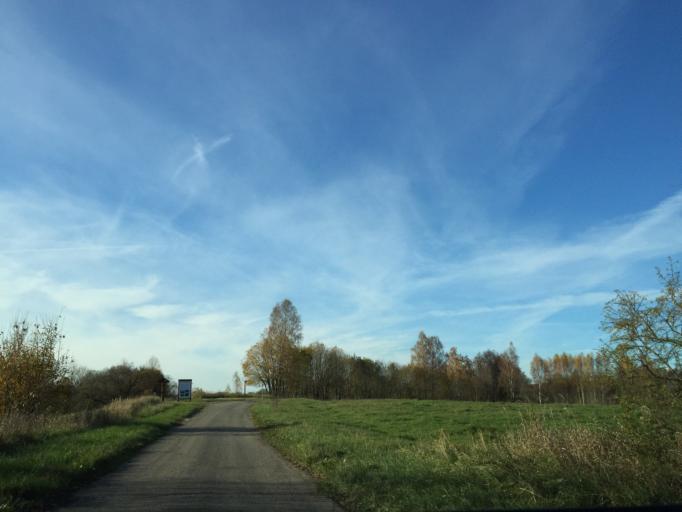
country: LV
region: Skriveri
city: Skriveri
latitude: 56.6189
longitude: 25.1423
